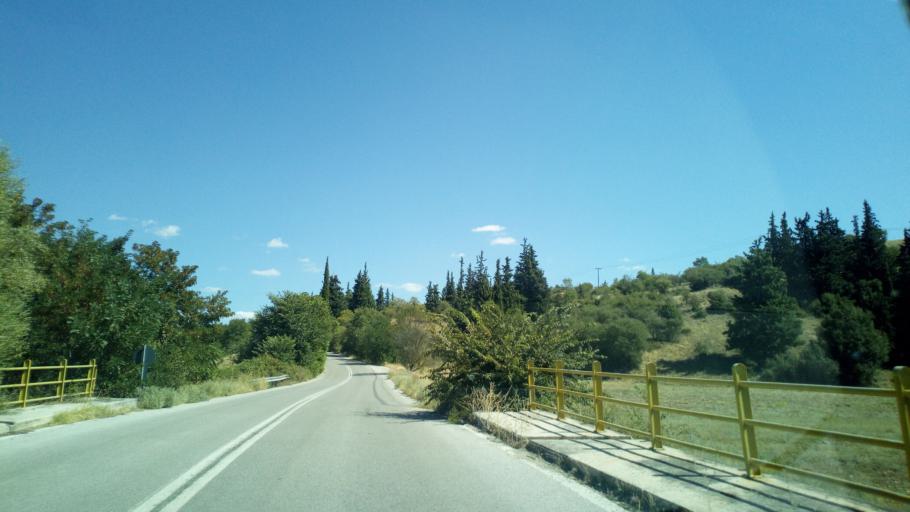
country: GR
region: Central Macedonia
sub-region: Nomos Thessalonikis
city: Kolchikon
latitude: 40.7773
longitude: 23.1055
